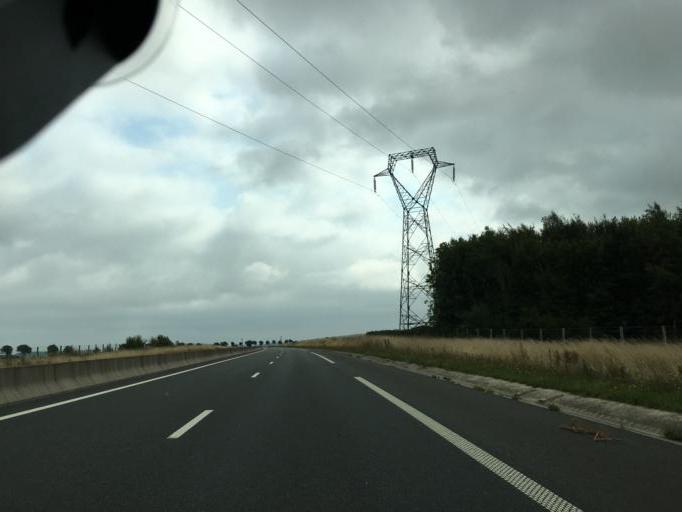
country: FR
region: Nord-Pas-de-Calais
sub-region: Departement du Pas-de-Calais
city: Montreuil
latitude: 50.4257
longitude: 1.7757
